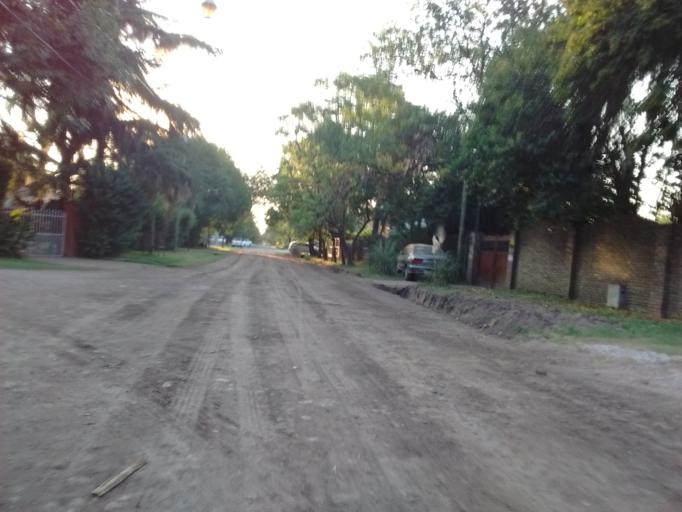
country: AR
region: Santa Fe
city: Funes
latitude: -32.9218
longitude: -60.8315
